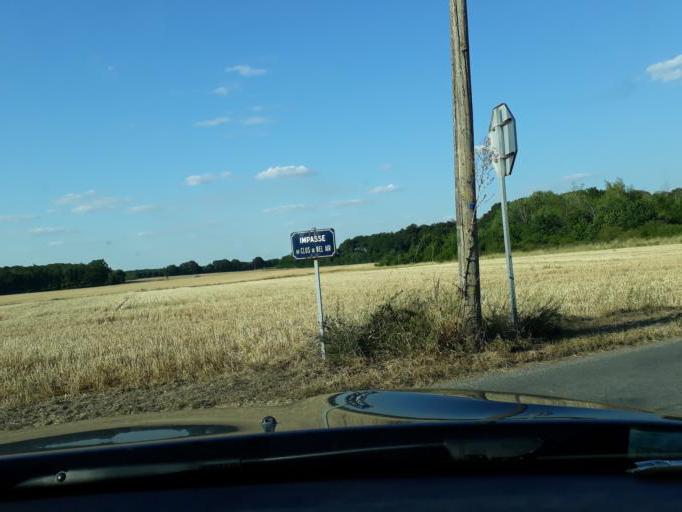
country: FR
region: Centre
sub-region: Departement du Loiret
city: Saint-Ay
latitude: 47.8870
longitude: 1.7367
